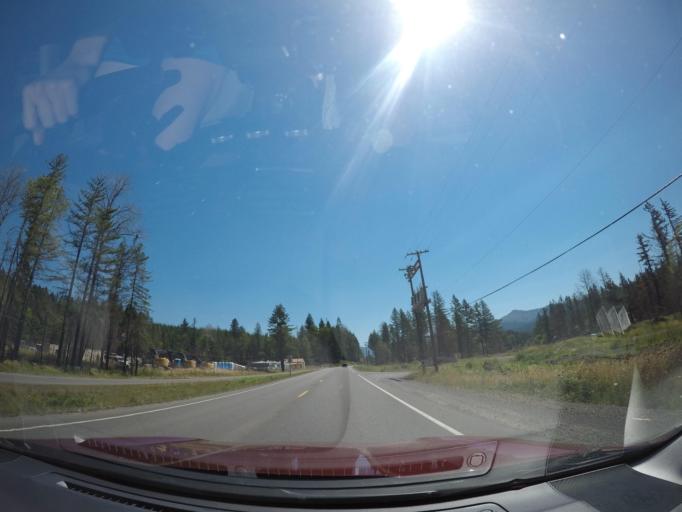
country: US
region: Oregon
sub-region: Linn County
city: Mill City
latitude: 44.7570
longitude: -122.4371
